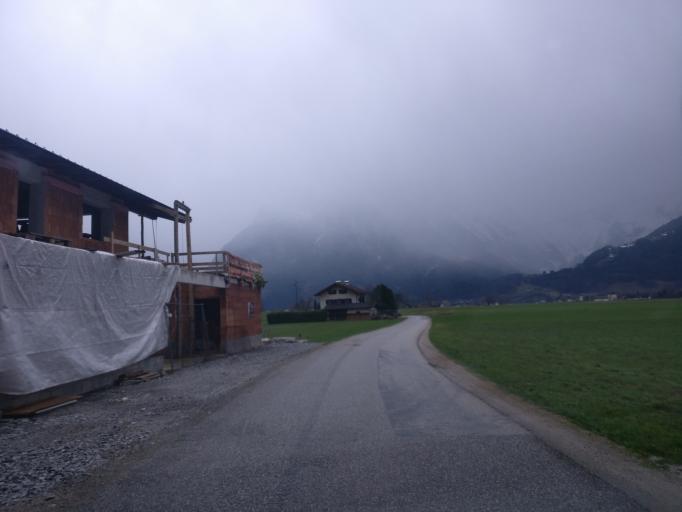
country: AT
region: Salzburg
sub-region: Politischer Bezirk Hallein
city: Golling an der Salzach
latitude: 47.6251
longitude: 13.1724
